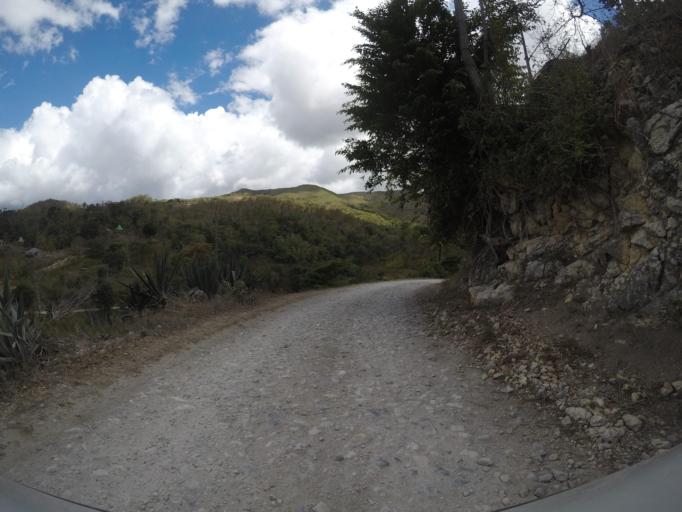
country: TL
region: Baucau
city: Baucau
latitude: -8.5256
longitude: 126.6931
